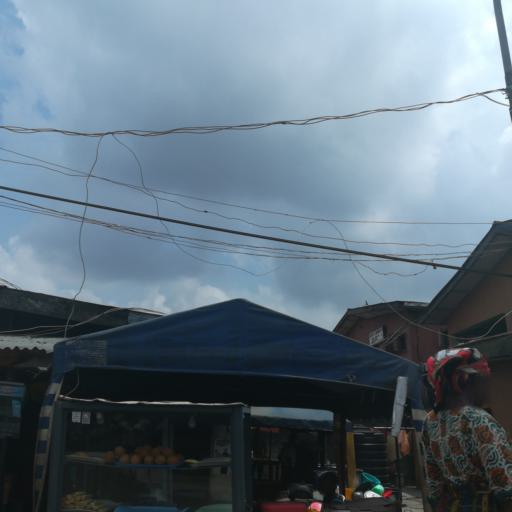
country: NG
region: Lagos
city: Ojota
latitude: 6.5855
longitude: 3.3797
